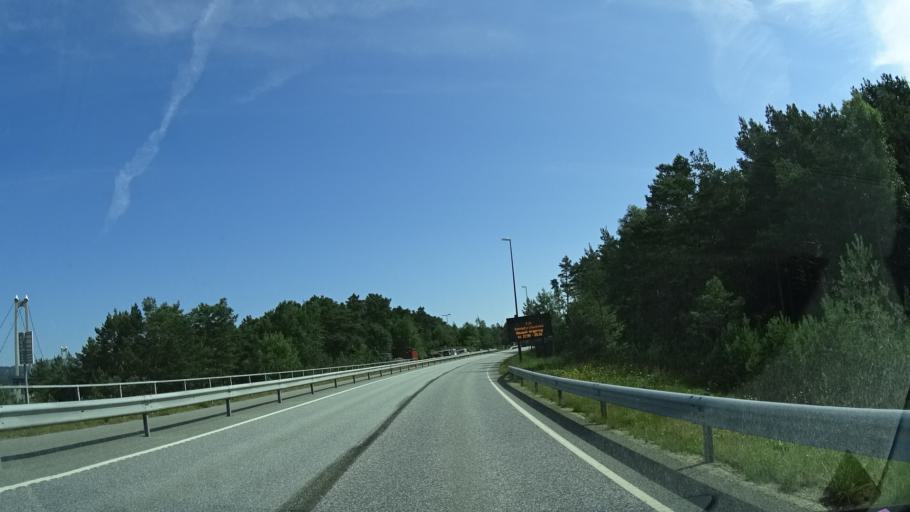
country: NO
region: Hordaland
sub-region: Stord
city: Sagvag
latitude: 59.7398
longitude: 5.4007
